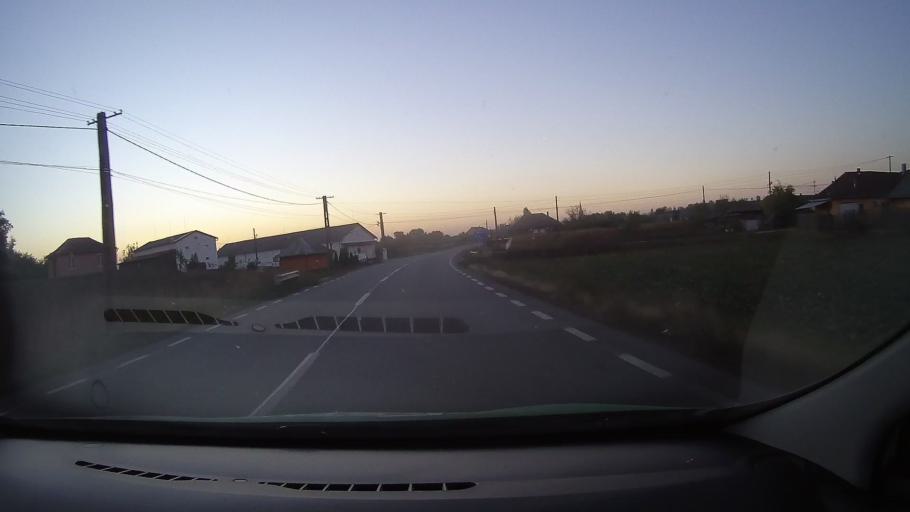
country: RO
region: Bihor
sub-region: Comuna Tarcea
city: Tarcea
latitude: 47.4549
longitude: 22.1773
